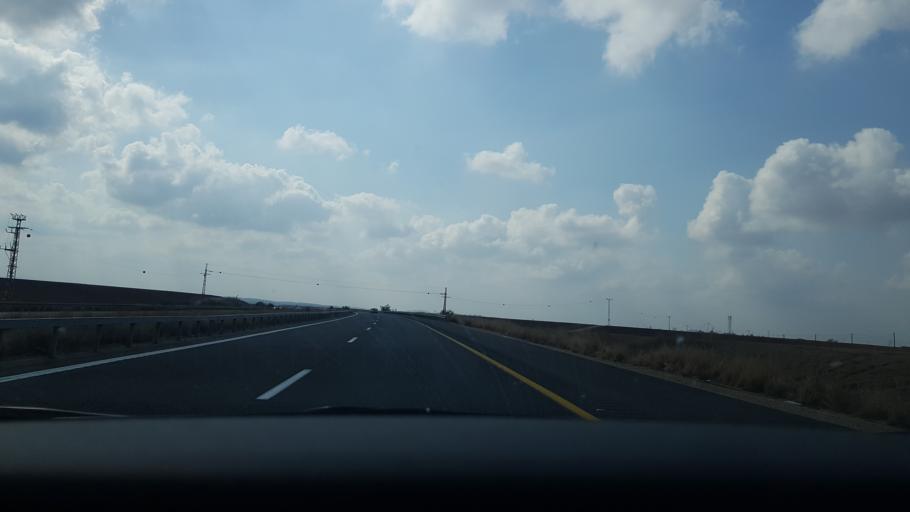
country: IL
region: Southern District
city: Qiryat Gat
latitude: 31.6767
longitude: 34.8062
